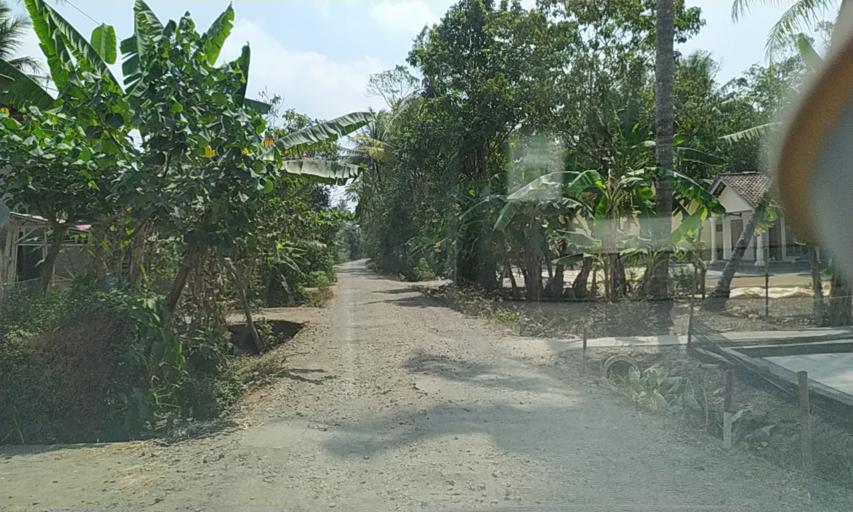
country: ID
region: Central Java
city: Kemantren Satu
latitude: -7.5443
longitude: 108.9061
